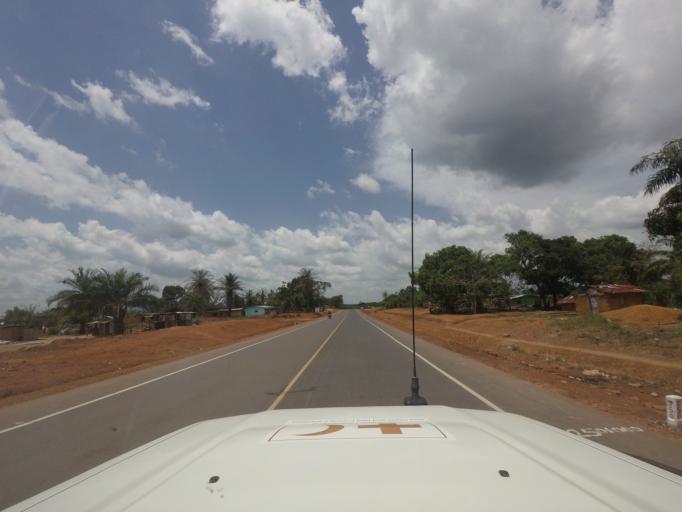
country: LR
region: Nimba
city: Sanniquellie
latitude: 7.2467
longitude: -8.9825
